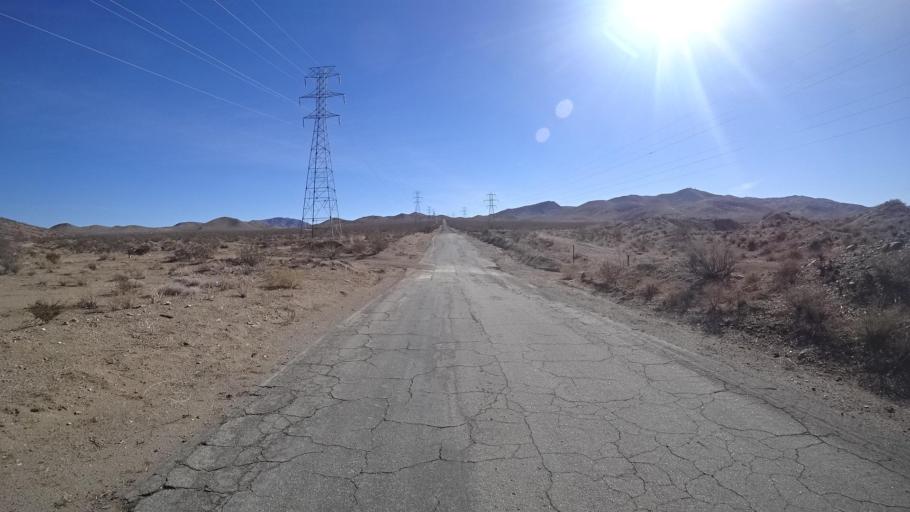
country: US
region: California
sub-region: Kern County
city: Ridgecrest
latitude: 35.3932
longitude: -117.6701
